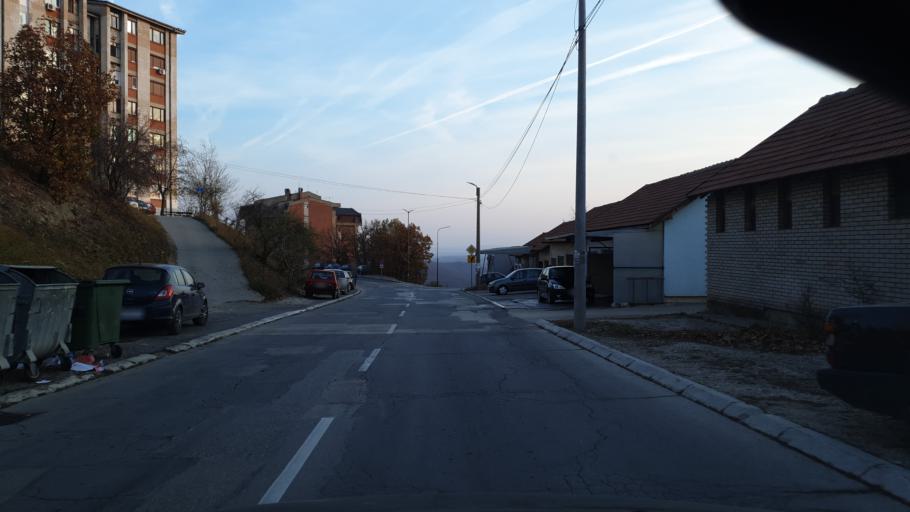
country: RS
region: Central Serbia
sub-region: Borski Okrug
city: Bor
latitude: 44.0563
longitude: 22.0953
